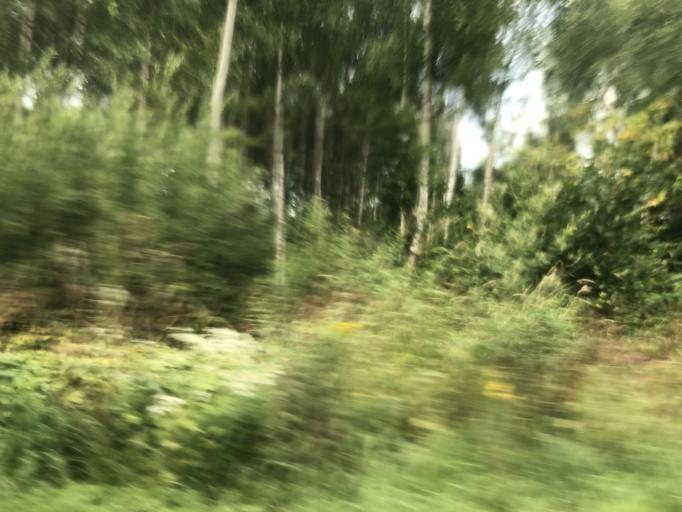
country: LV
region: Vecumnieki
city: Vecumnieki
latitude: 56.4571
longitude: 24.6517
